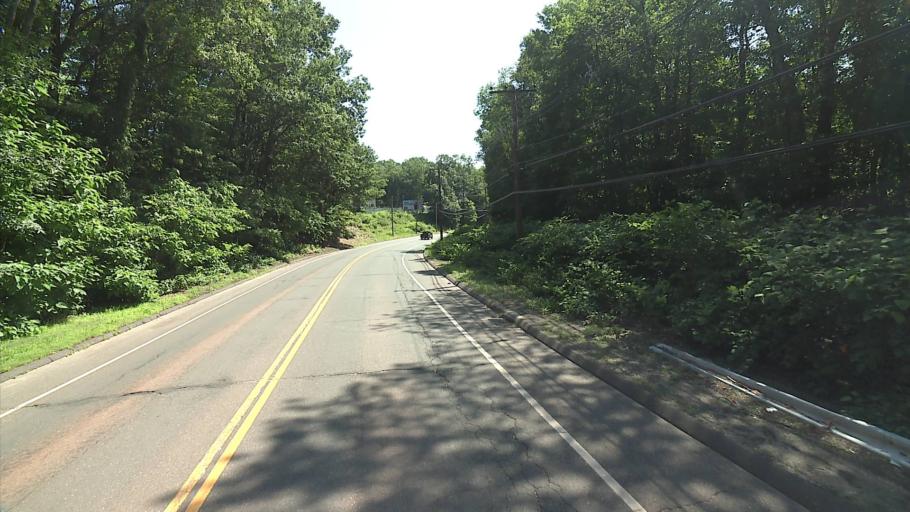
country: US
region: Connecticut
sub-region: Litchfield County
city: Terryville
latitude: 41.6700
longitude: -72.9872
